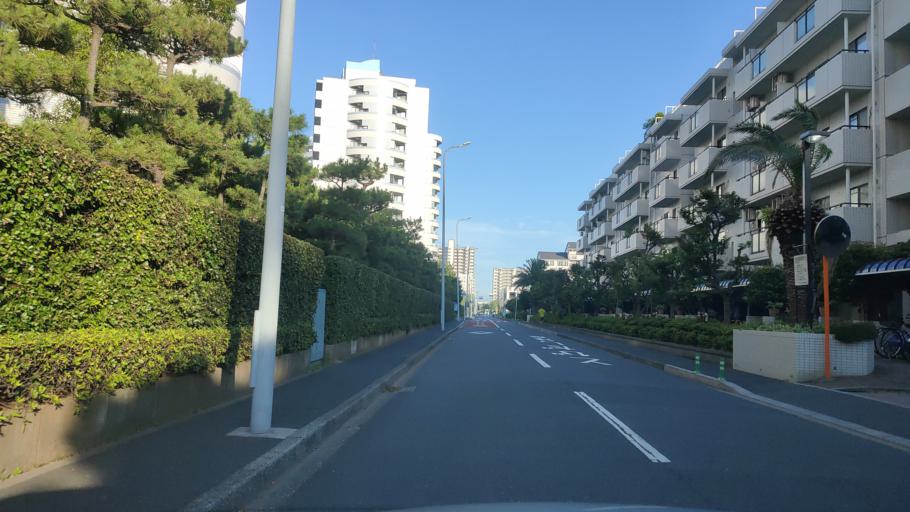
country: JP
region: Tokyo
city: Urayasu
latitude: 35.6468
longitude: 139.9228
